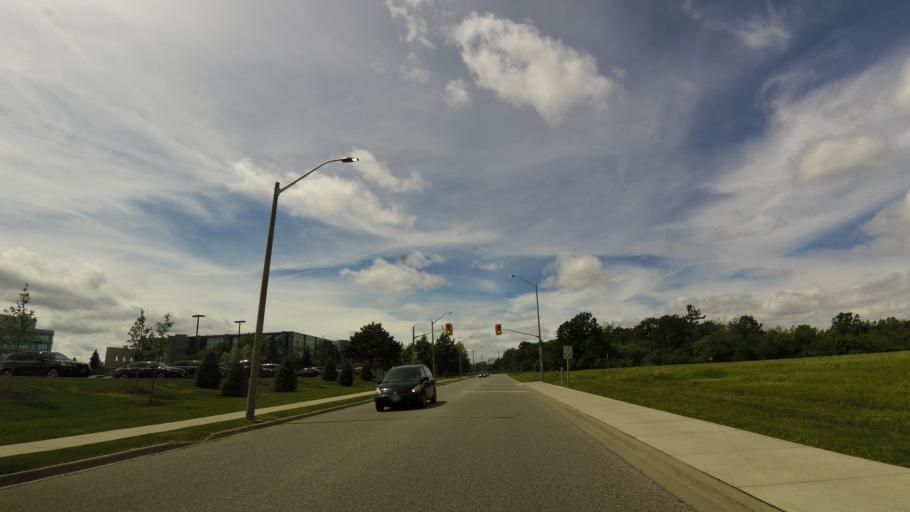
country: CA
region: Ontario
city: Mississauga
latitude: 43.5148
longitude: -79.6681
